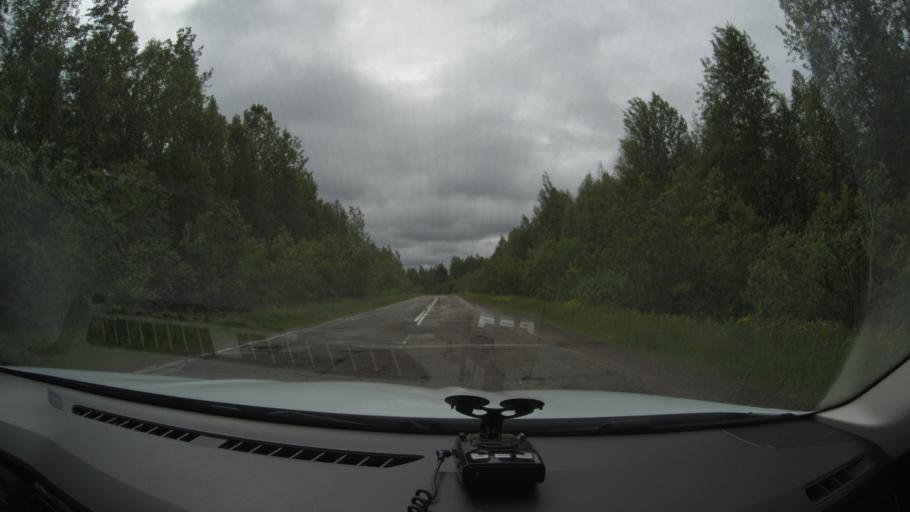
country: RU
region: Komi Republic
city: Nizhniy Odes
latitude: 63.6419
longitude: 54.6500
